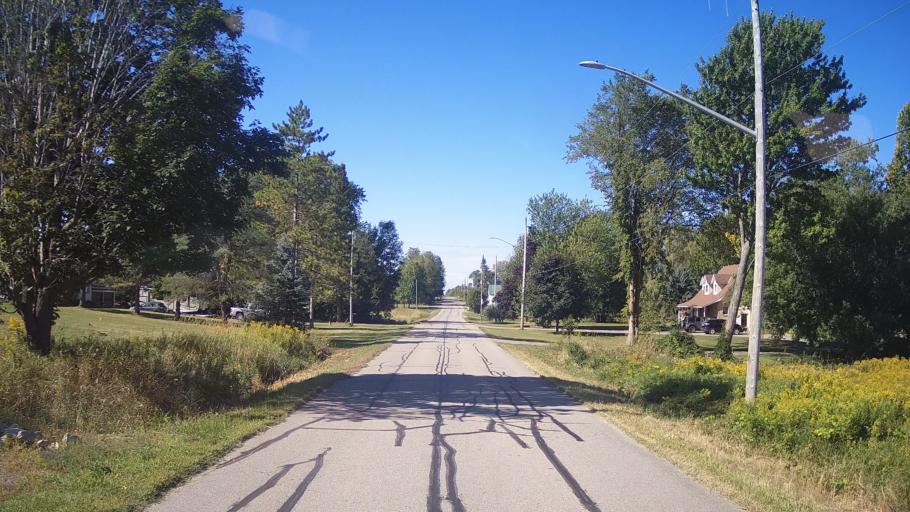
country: CA
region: Ontario
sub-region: Lanark County
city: Smiths Falls
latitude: 44.8395
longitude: -75.8824
